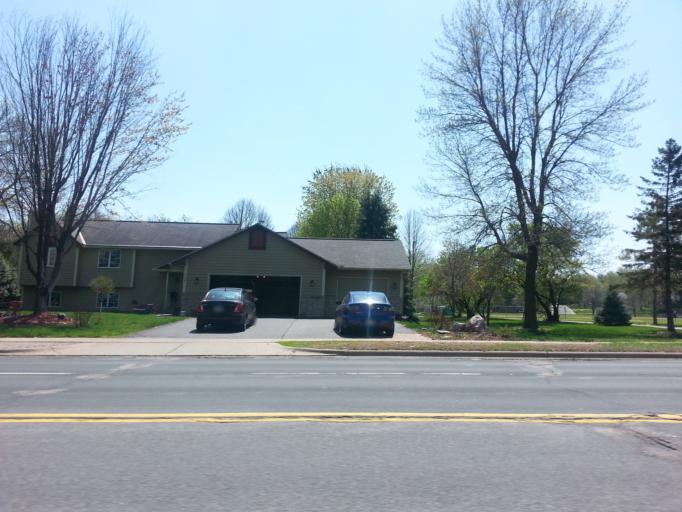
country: US
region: Minnesota
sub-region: Dakota County
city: Burnsville
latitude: 44.7549
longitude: -93.3095
